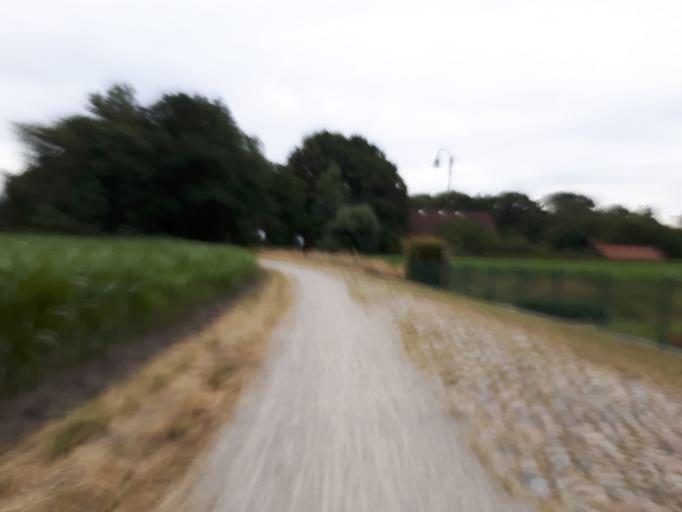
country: DE
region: Lower Saxony
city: Stuhr
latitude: 53.0333
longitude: 8.7071
